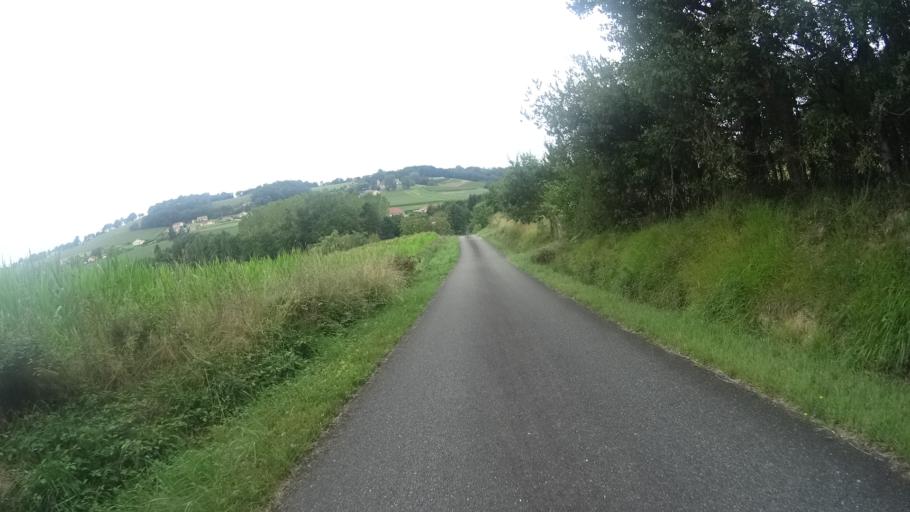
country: FR
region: Aquitaine
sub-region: Departement des Pyrenees-Atlantiques
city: Mont
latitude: 43.4850
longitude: -0.6940
